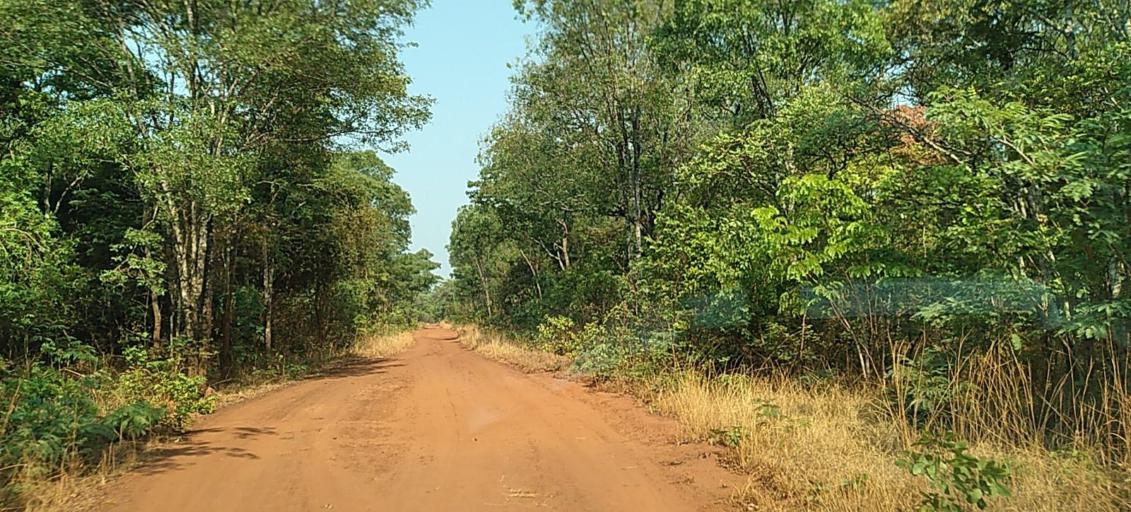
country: ZM
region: Copperbelt
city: Chingola
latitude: -12.8858
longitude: 27.4172
